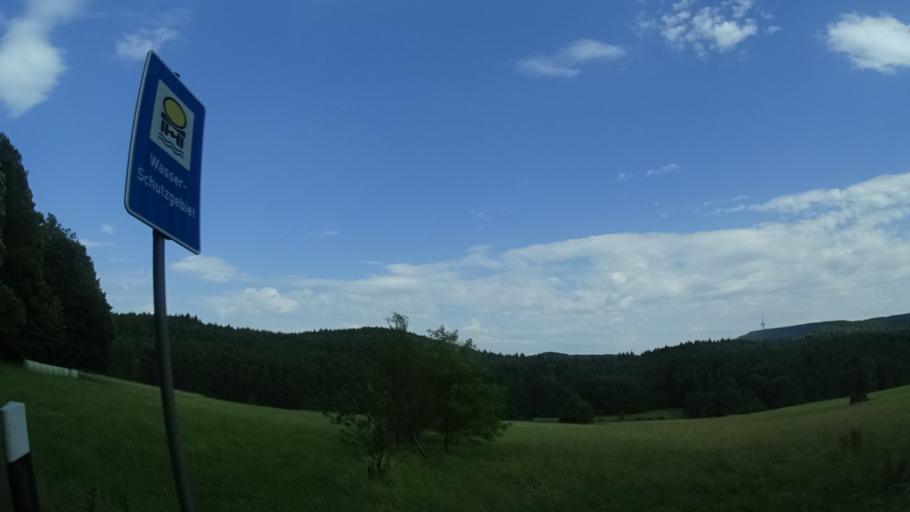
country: DE
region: Hesse
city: Haina
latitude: 51.0470
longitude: 8.9844
